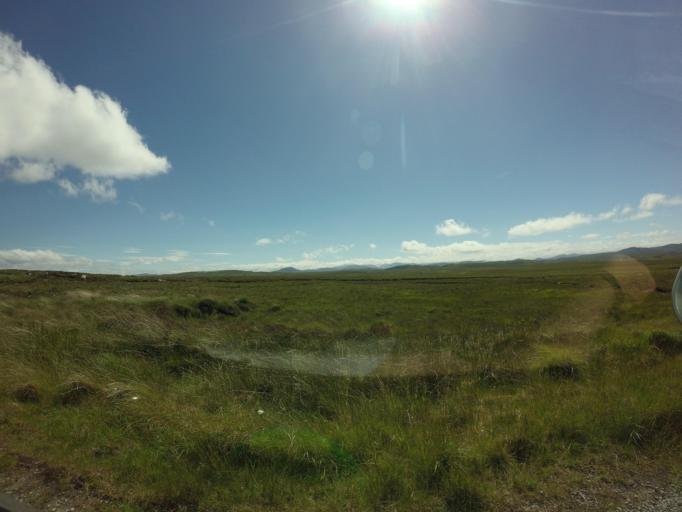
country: GB
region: Scotland
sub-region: Eilean Siar
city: Isle of Lewis
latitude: 58.1857
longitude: -6.6792
